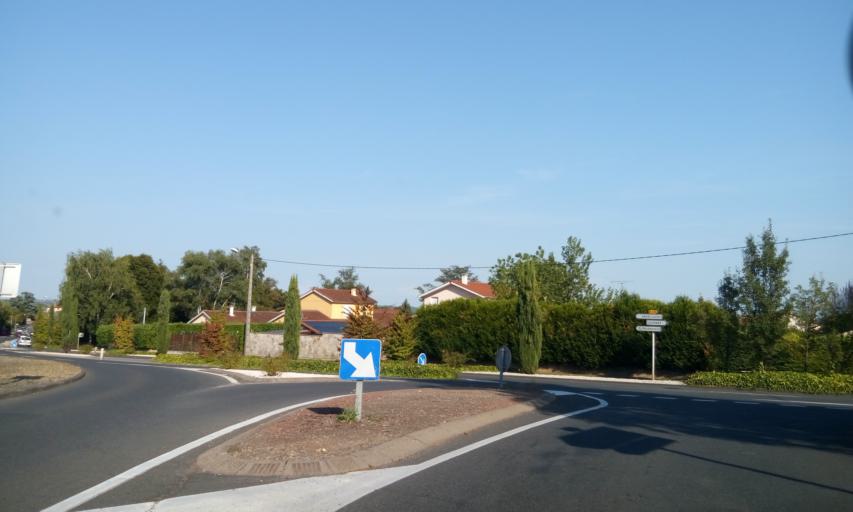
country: FR
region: Rhone-Alpes
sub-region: Departement du Rhone
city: Anse
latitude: 45.9308
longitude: 4.7095
